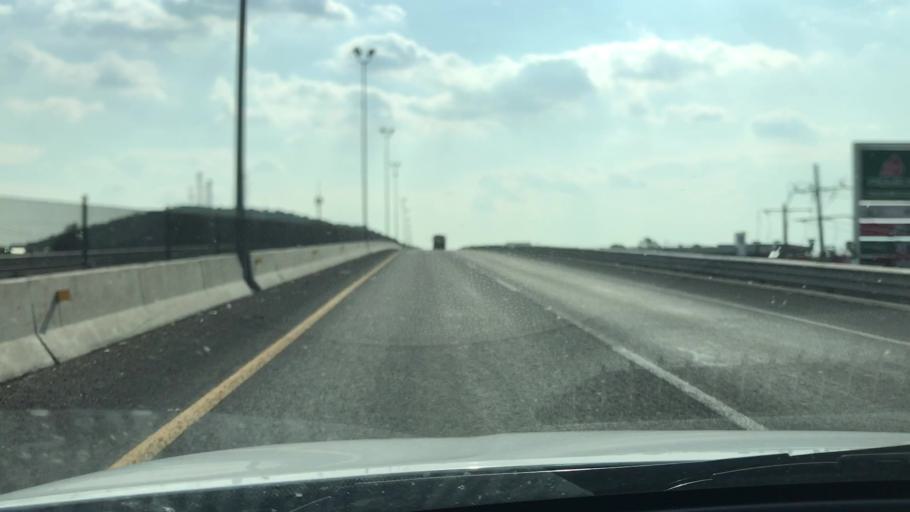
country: MX
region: Guanajuato
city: Salamanca
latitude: 20.5406
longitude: -101.2034
